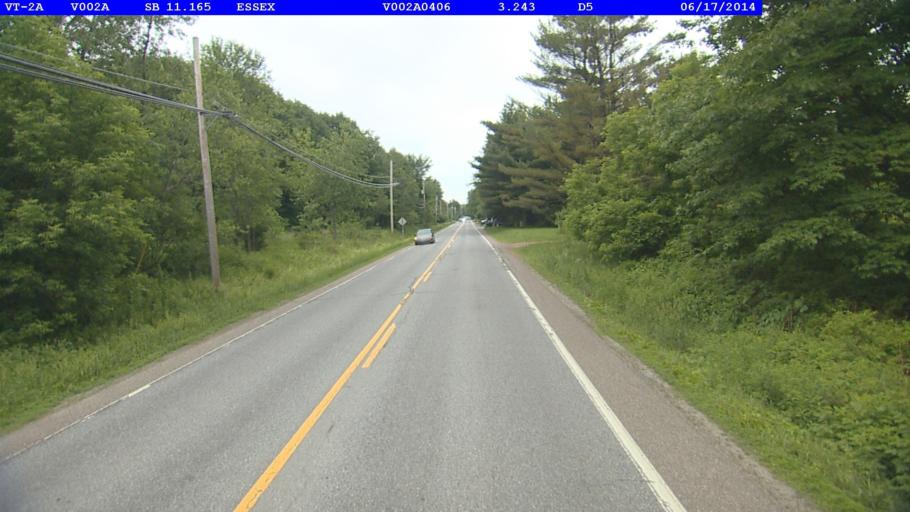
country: US
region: Vermont
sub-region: Chittenden County
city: Colchester
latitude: 44.5258
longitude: -73.1256
